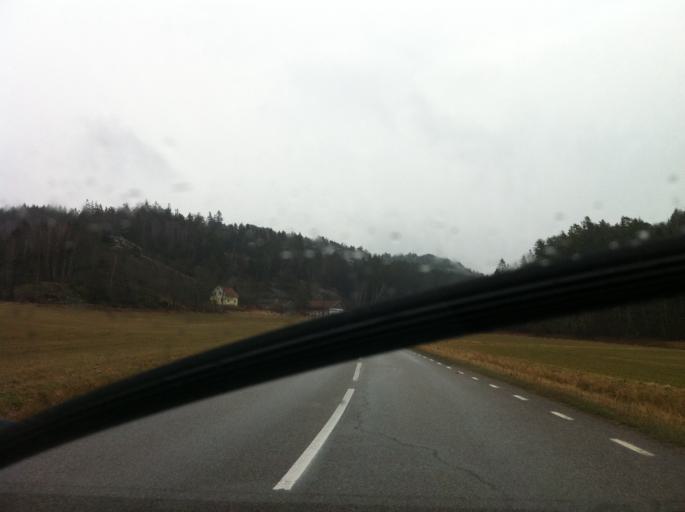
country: SE
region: Vaestra Goetaland
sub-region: Lysekils Kommun
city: Brastad
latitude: 58.4546
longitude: 11.4732
